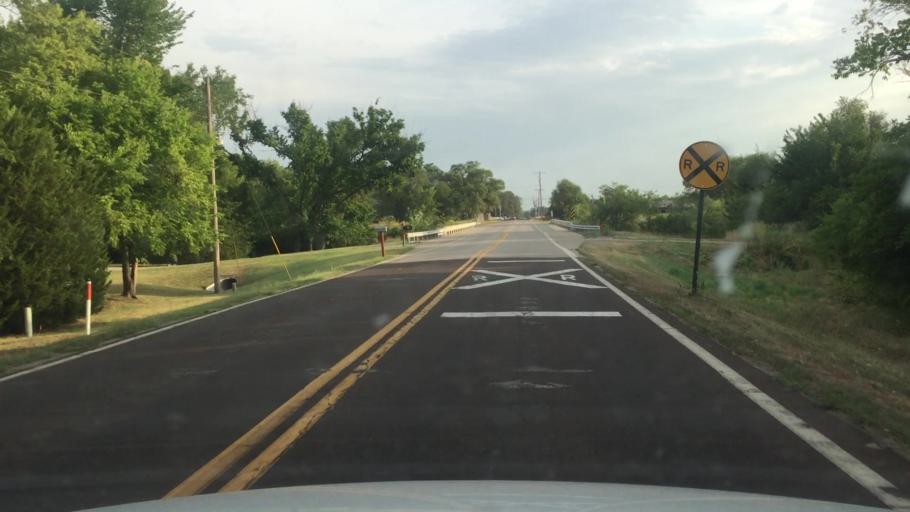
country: US
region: Kansas
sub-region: Shawnee County
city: Topeka
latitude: 39.0533
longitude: -95.6132
